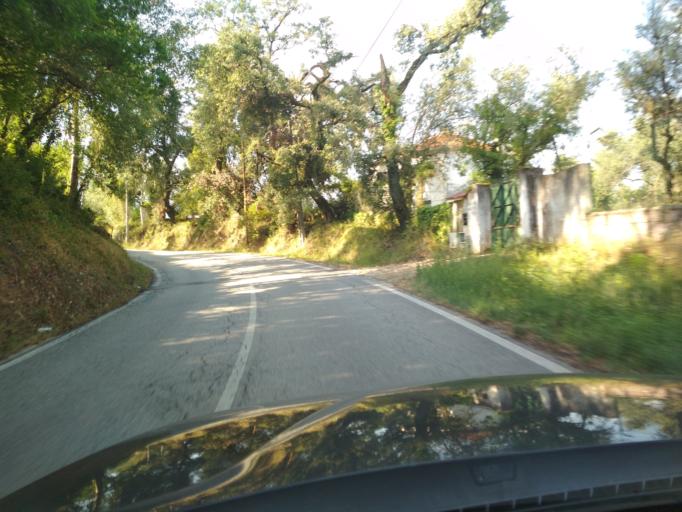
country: PT
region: Coimbra
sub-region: Condeixa-A-Nova
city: Condeixa-a-Nova
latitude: 40.1461
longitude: -8.4676
